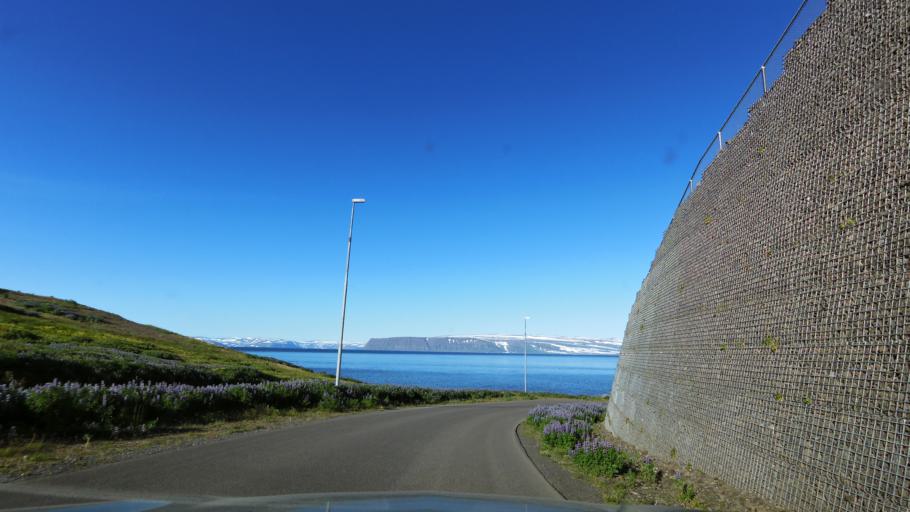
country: IS
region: Westfjords
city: Isafjoerdur
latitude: 66.1627
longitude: -23.2517
